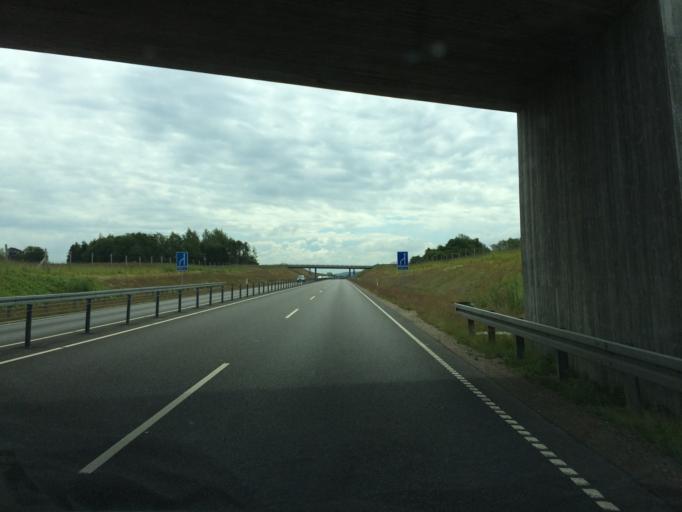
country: DK
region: Zealand
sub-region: Odsherred Kommune
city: Hojby
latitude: 55.8618
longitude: 11.5928
